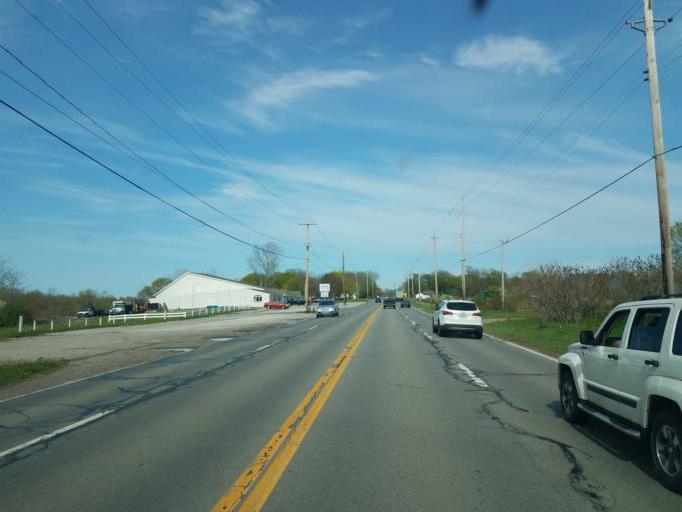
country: US
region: Ohio
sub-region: Lake County
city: Perry
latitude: 41.7776
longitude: -81.1547
